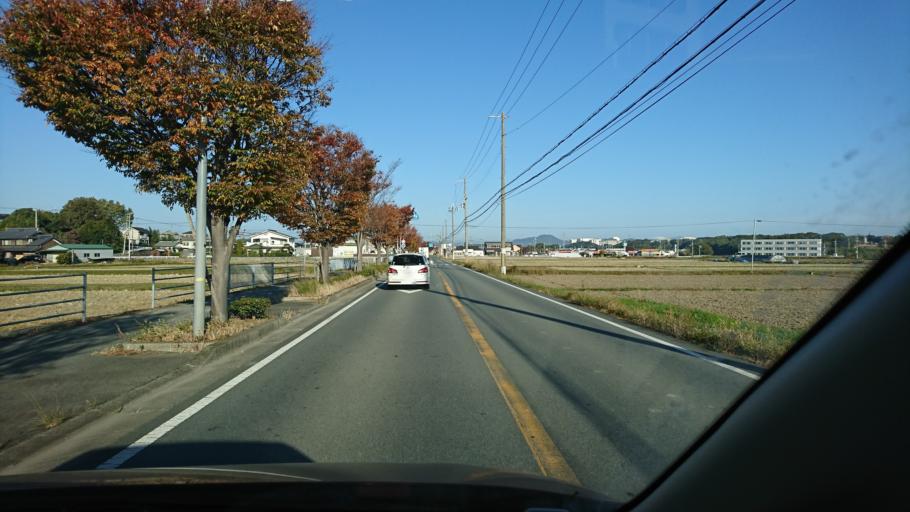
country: JP
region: Hyogo
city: Kakogawacho-honmachi
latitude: 34.7591
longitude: 134.8873
